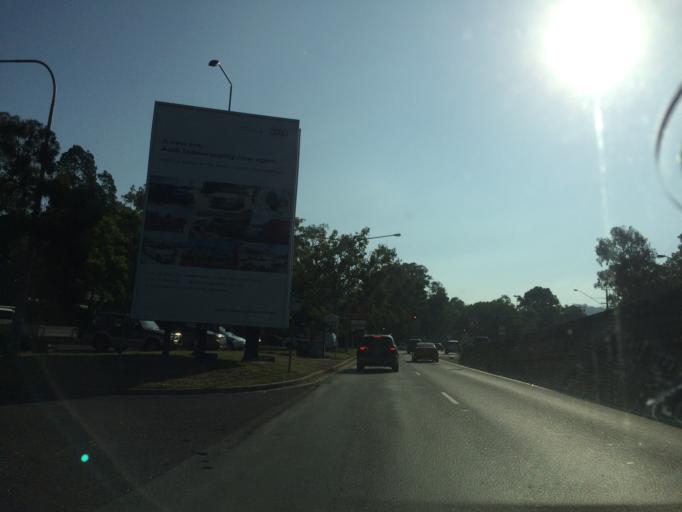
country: AU
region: Queensland
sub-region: Brisbane
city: Toowong
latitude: -27.4783
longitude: 152.9839
